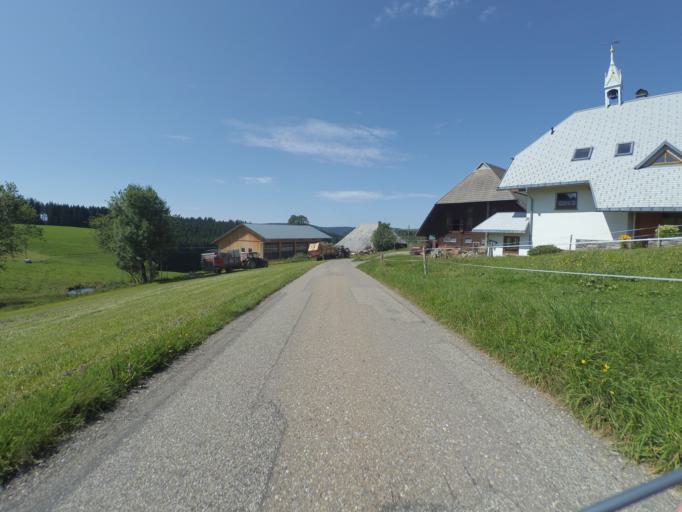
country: DE
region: Baden-Wuerttemberg
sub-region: Freiburg Region
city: Gutenbach
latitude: 48.0481
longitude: 8.1628
